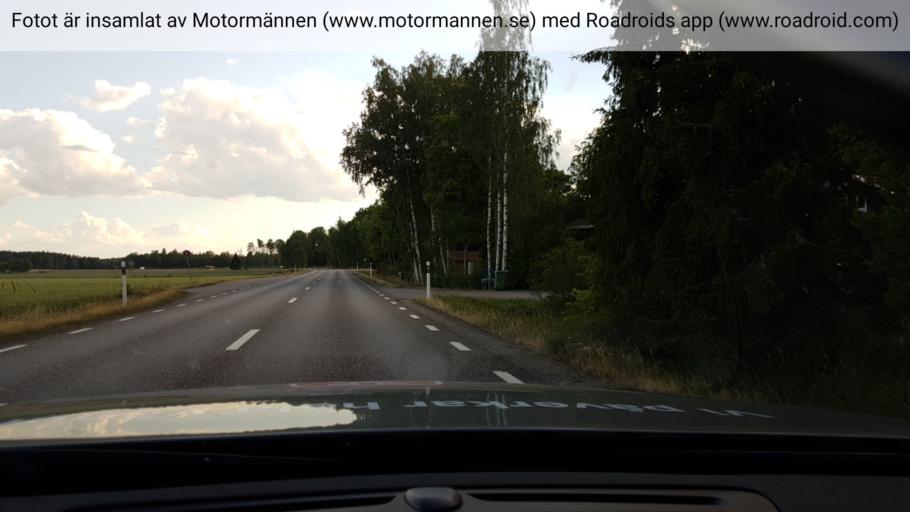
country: SE
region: Uppsala
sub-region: Enkopings Kommun
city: Irsta
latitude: 59.8048
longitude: 16.9087
